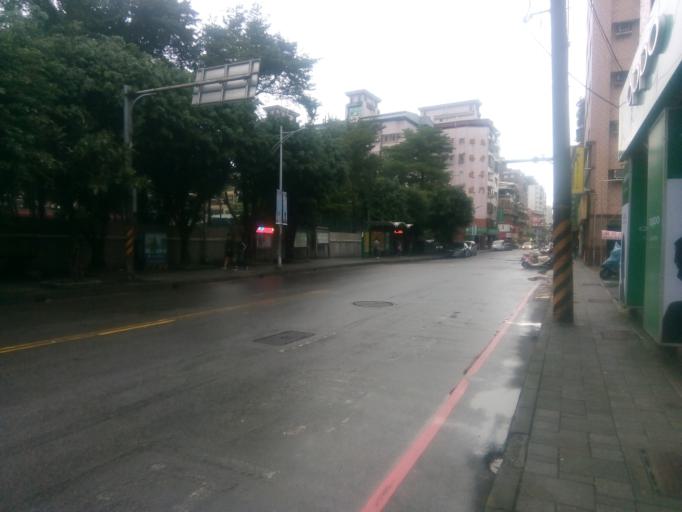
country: TW
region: Taiwan
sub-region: Keelung
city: Keelung
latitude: 25.0661
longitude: 121.6617
